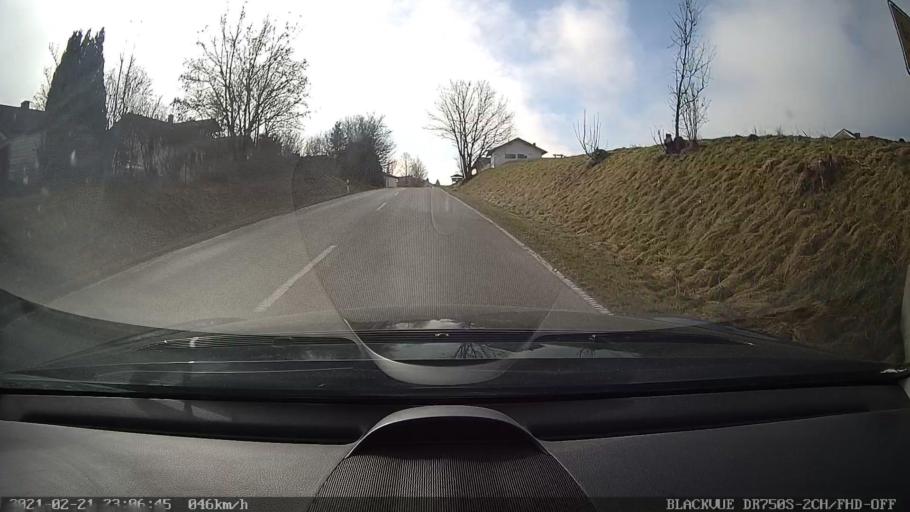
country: DE
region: Bavaria
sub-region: Upper Bavaria
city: Griesstatt
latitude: 47.9981
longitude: 12.1790
